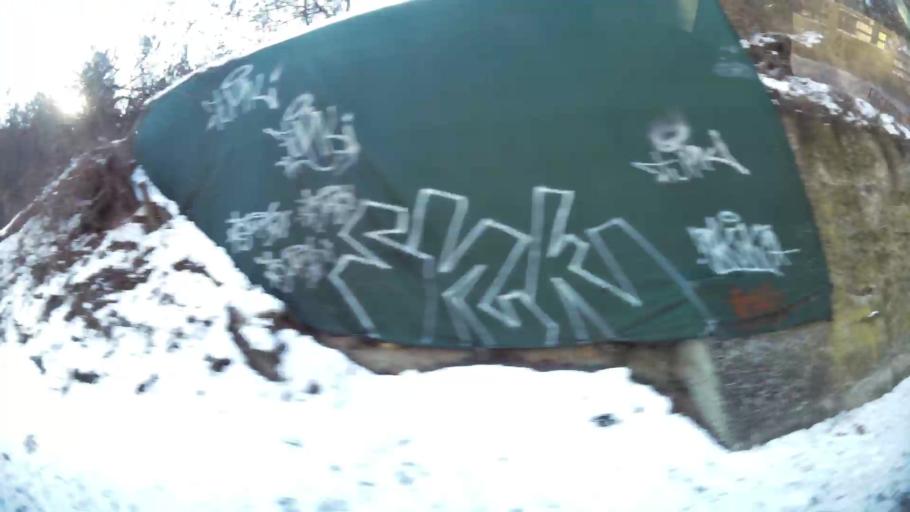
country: MK
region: Karpos
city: Skopje
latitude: 41.9810
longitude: 21.4212
